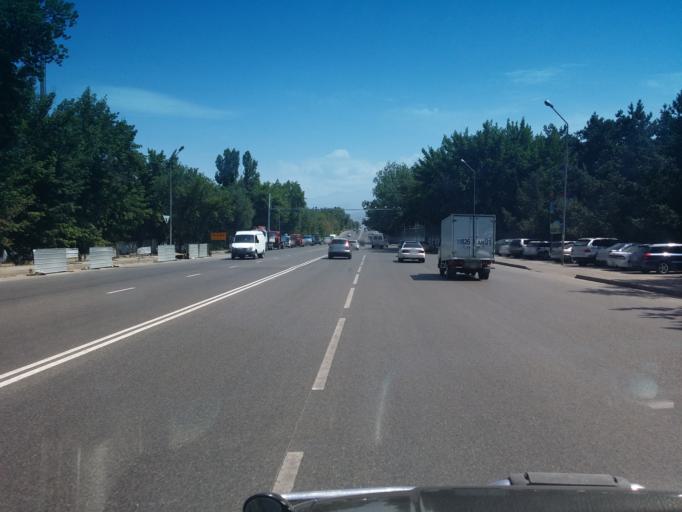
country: KZ
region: Almaty Oblysy
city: Pervomayskiy
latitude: 43.3443
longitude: 76.9728
